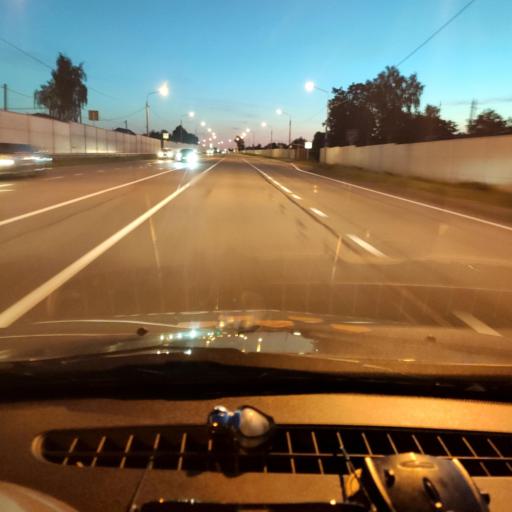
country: RU
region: Belgorod
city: Gubkin
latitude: 51.1856
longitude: 37.3811
